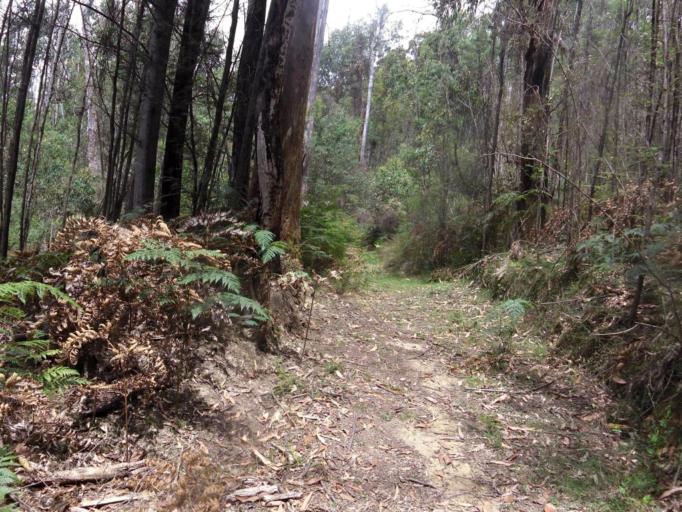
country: AU
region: Victoria
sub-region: Yarra Ranges
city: Healesville
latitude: -37.4340
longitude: 145.5736
